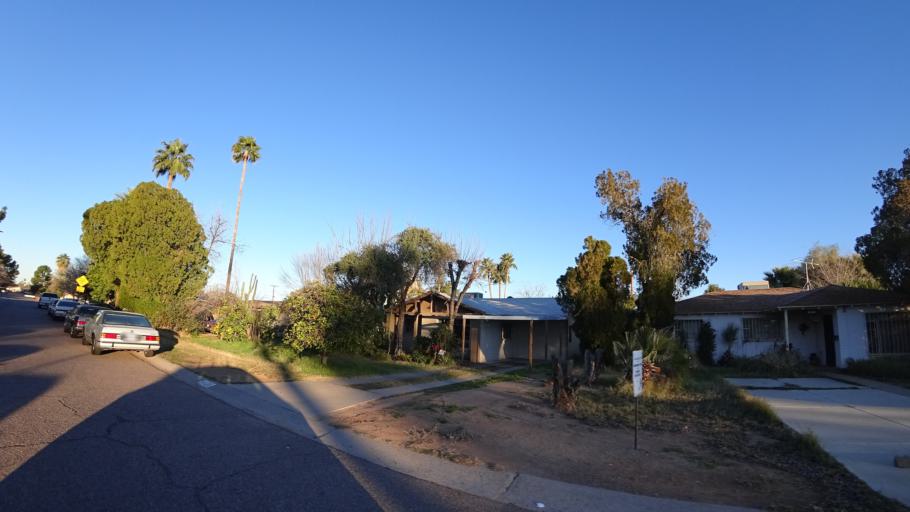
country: US
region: Arizona
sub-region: Maricopa County
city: Paradise Valley
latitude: 33.4844
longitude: -111.9873
